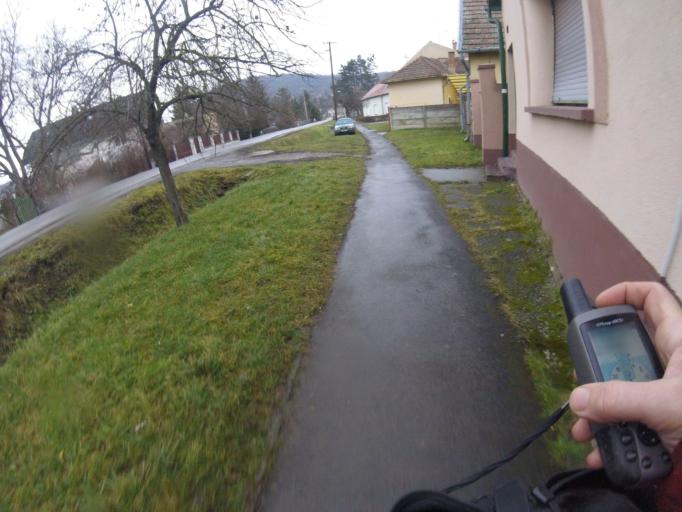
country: HU
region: Pest
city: Veroce
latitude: 47.8285
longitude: 19.0393
